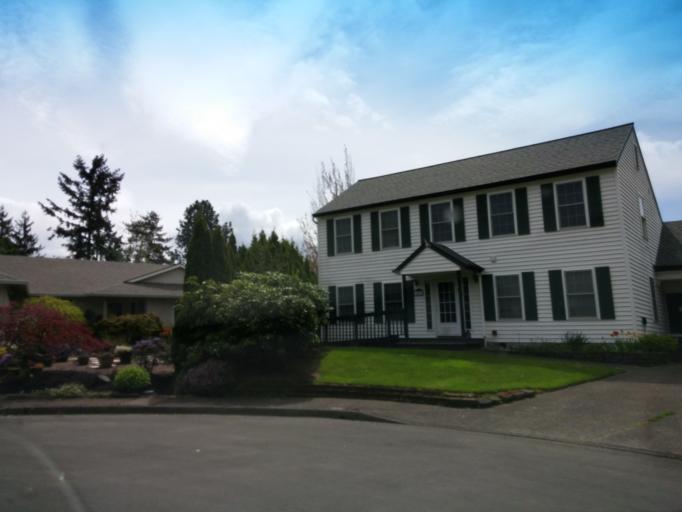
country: US
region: Oregon
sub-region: Washington County
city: Cedar Hills
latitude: 45.5062
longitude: -122.8140
